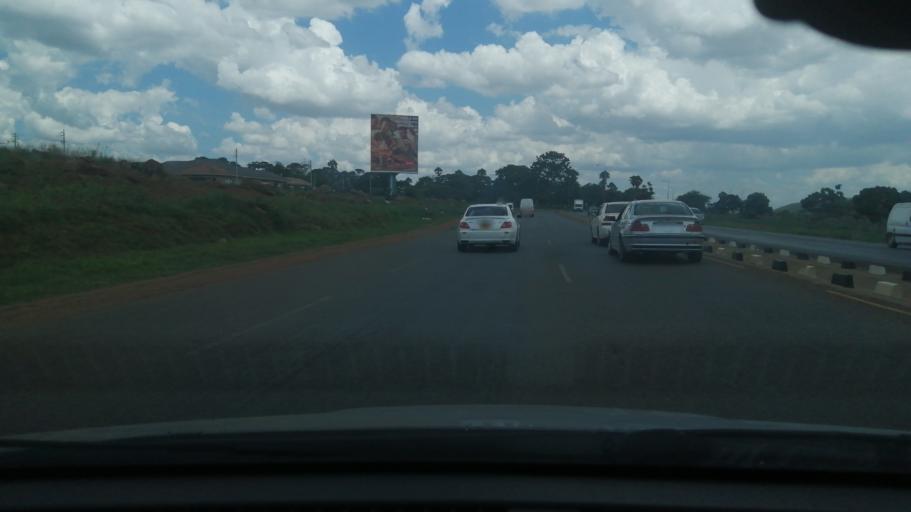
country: ZW
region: Harare
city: Harare
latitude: -17.8187
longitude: 30.9387
